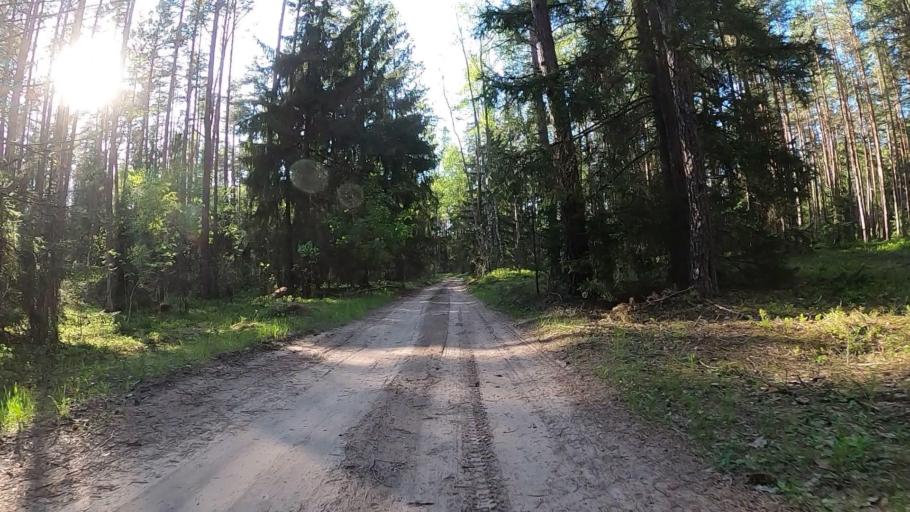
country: LV
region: Baldone
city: Baldone
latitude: 56.7665
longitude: 24.3688
